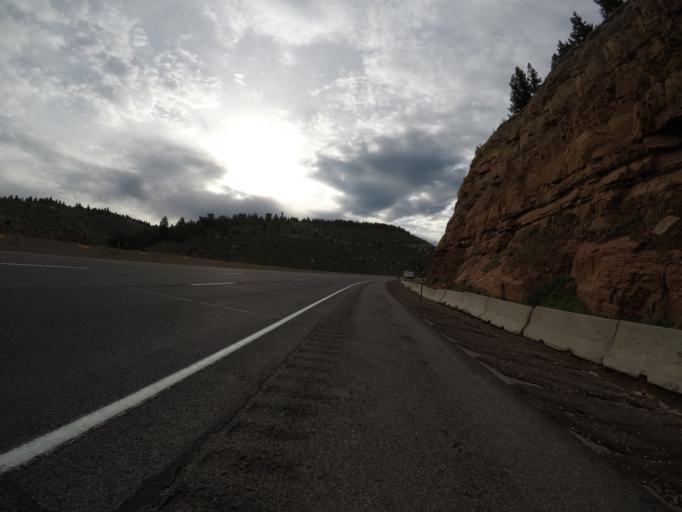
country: US
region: Wyoming
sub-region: Albany County
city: Laramie
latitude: 41.2722
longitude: -105.4842
